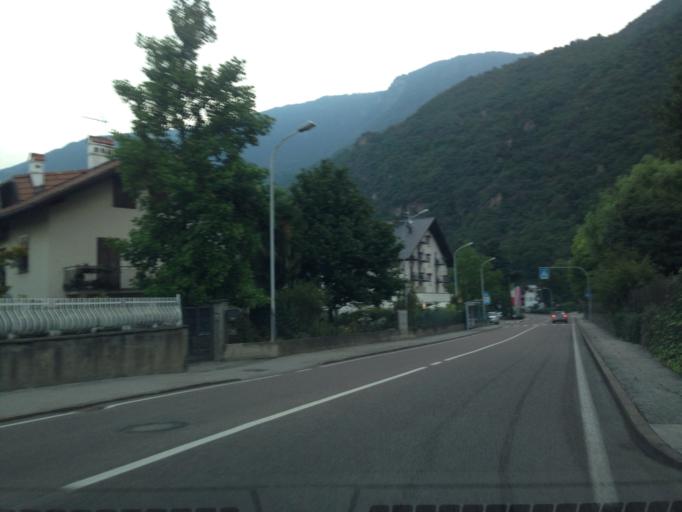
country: IT
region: Trentino-Alto Adige
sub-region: Bolzano
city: Laives
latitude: 46.4288
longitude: 11.3423
